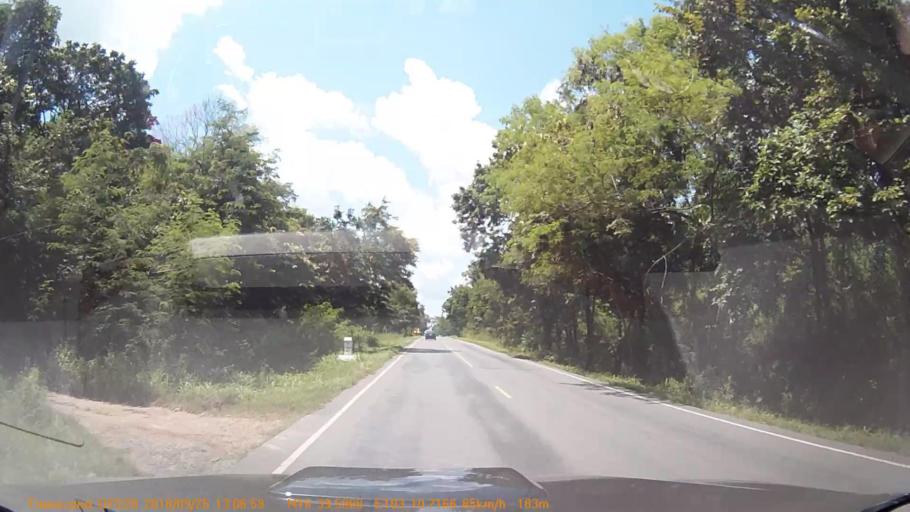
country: TH
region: Kalasin
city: Huai Mek
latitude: 16.6599
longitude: 103.1786
